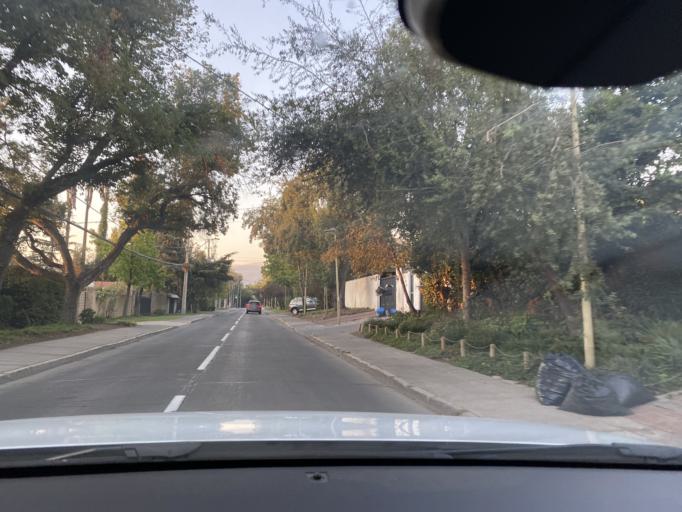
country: CL
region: Santiago Metropolitan
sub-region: Provincia de Santiago
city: Villa Presidente Frei, Nunoa, Santiago, Chile
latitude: -33.3965
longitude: -70.5224
